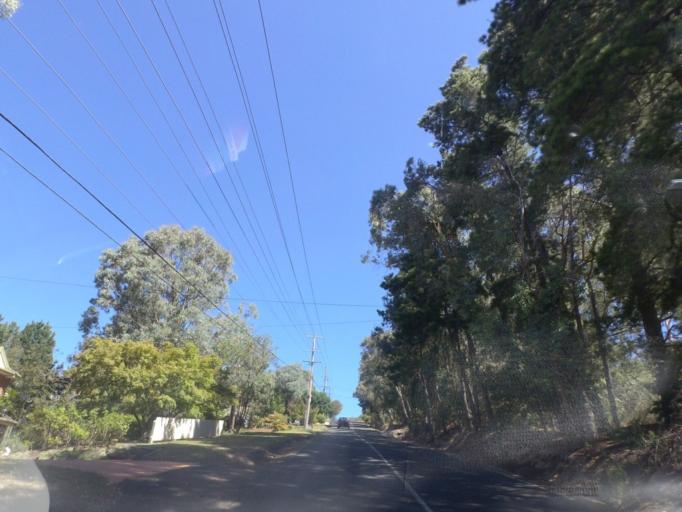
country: AU
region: Victoria
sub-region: Manningham
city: Park Orchards
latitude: -37.7965
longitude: 145.2163
